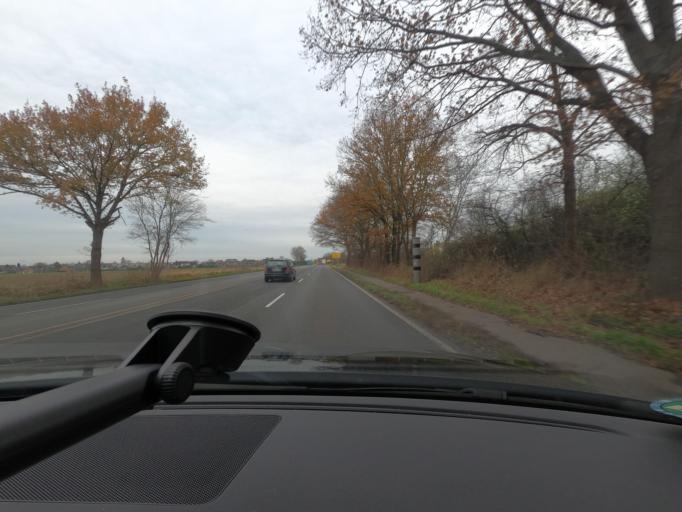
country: DE
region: North Rhine-Westphalia
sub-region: Regierungsbezirk Dusseldorf
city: Hochfeld
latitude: 51.3574
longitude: 6.6954
